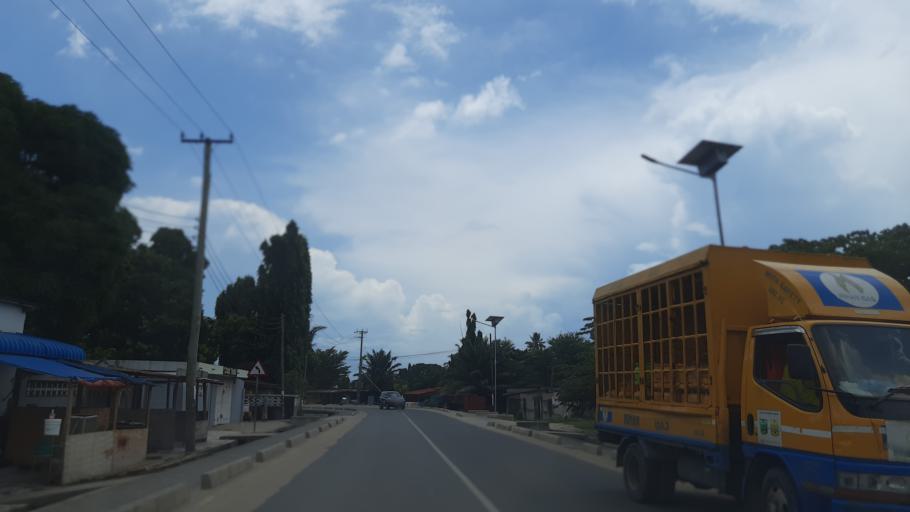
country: TZ
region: Dar es Salaam
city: Magomeni
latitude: -6.7729
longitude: 39.2300
